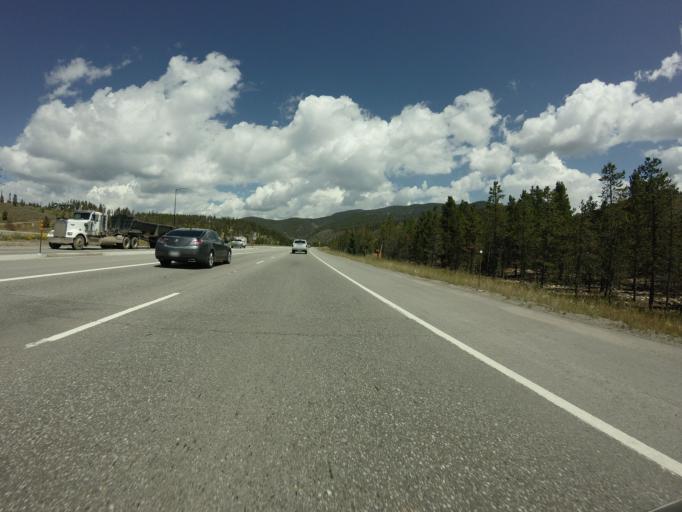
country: US
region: Colorado
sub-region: Summit County
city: Breckenridge
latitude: 39.5409
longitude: -106.0416
